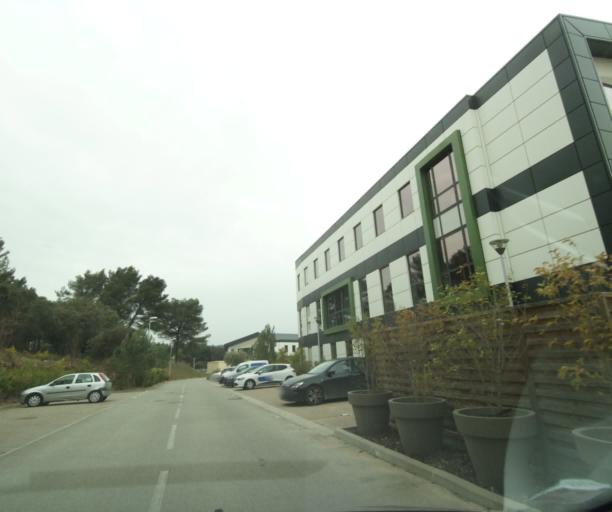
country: FR
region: Provence-Alpes-Cote d'Azur
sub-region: Departement des Bouches-du-Rhone
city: Meyreuil
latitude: 43.4901
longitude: 5.5300
